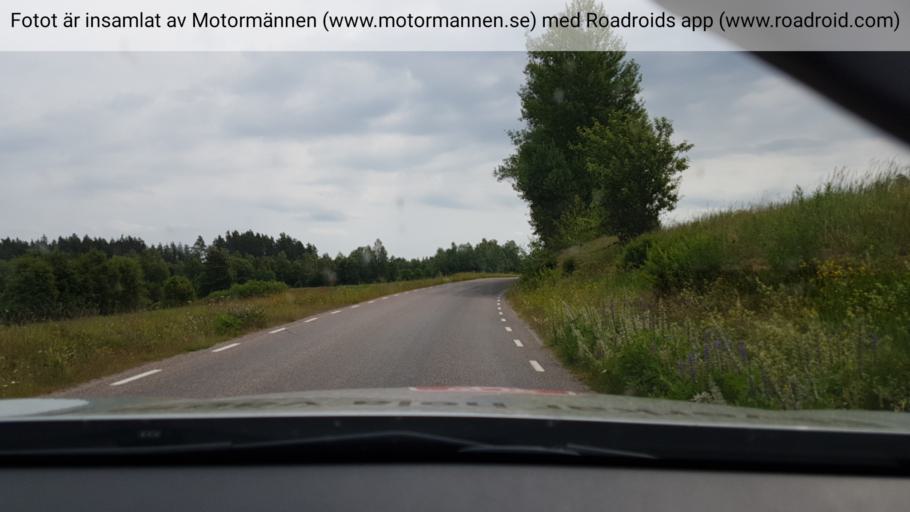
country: SE
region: Vaestra Goetaland
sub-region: Tidaholms Kommun
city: Tidaholm
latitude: 58.0730
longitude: 13.9221
